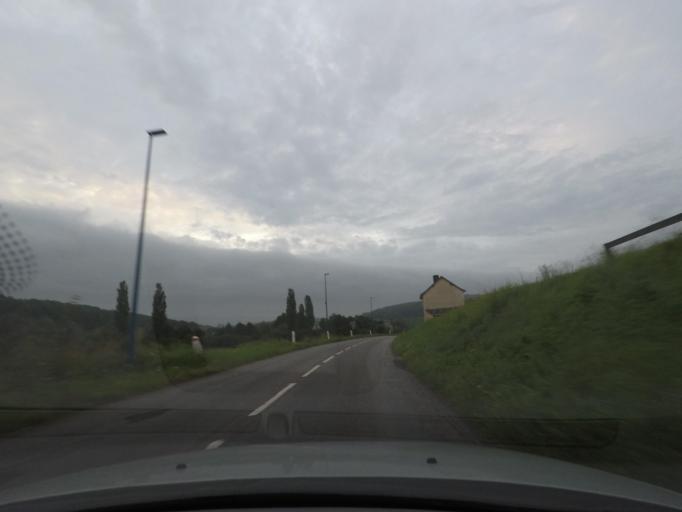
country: FR
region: Haute-Normandie
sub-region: Departement de la Seine-Maritime
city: Fontaine-le-Bourg
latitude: 49.5597
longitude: 1.1402
